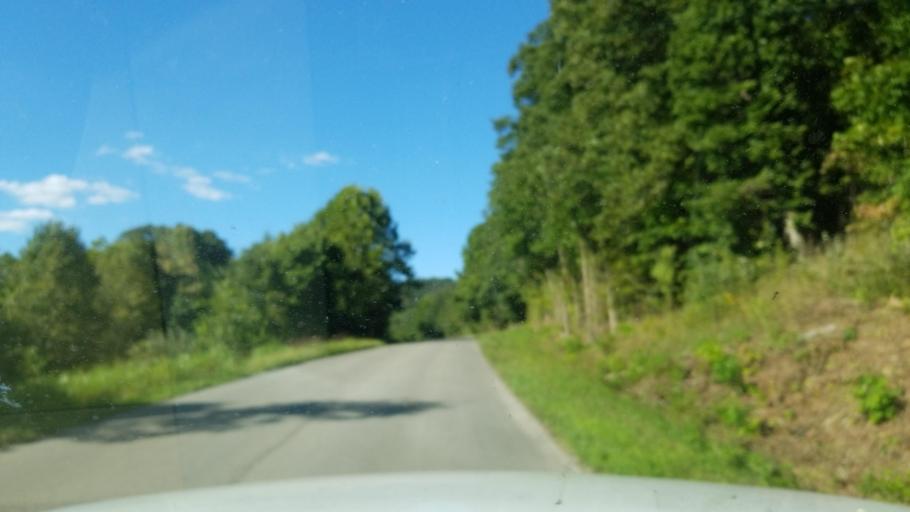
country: US
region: Illinois
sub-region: Hardin County
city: Elizabethtown
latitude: 37.5913
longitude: -88.3656
